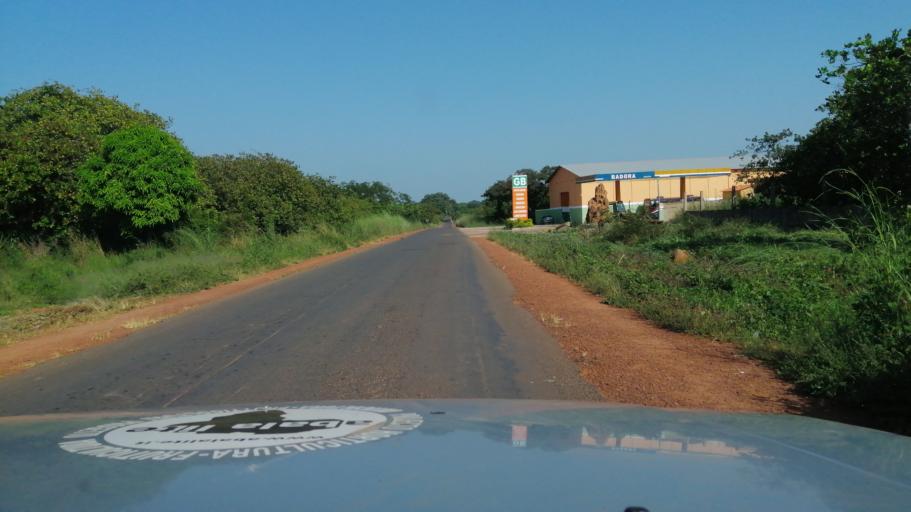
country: GW
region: Bissau
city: Bissau
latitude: 11.9589
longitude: -15.5345
